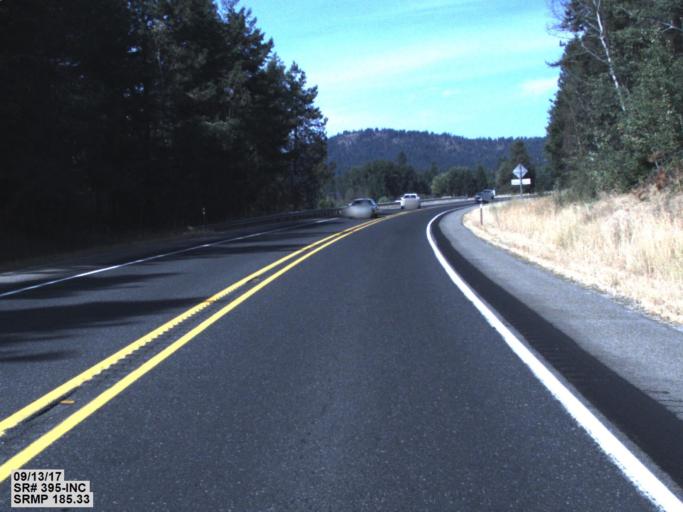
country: US
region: Washington
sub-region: Spokane County
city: Deer Park
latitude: 47.9944
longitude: -117.5683
